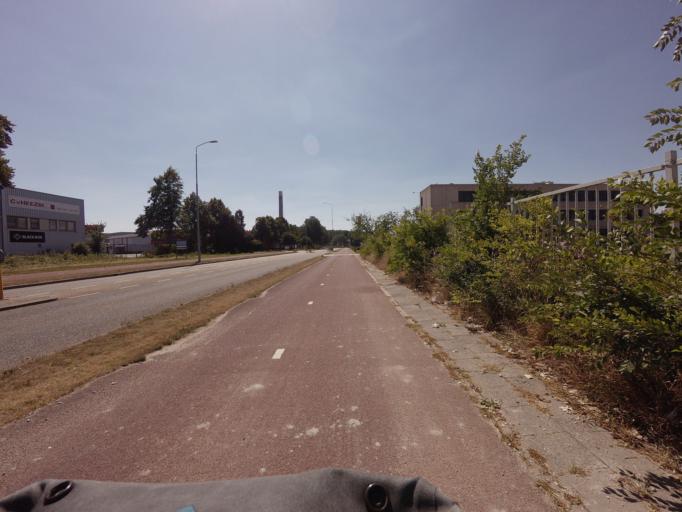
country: NL
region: Utrecht
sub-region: Stichtse Vecht
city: Maarssen
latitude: 52.1082
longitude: 5.0648
